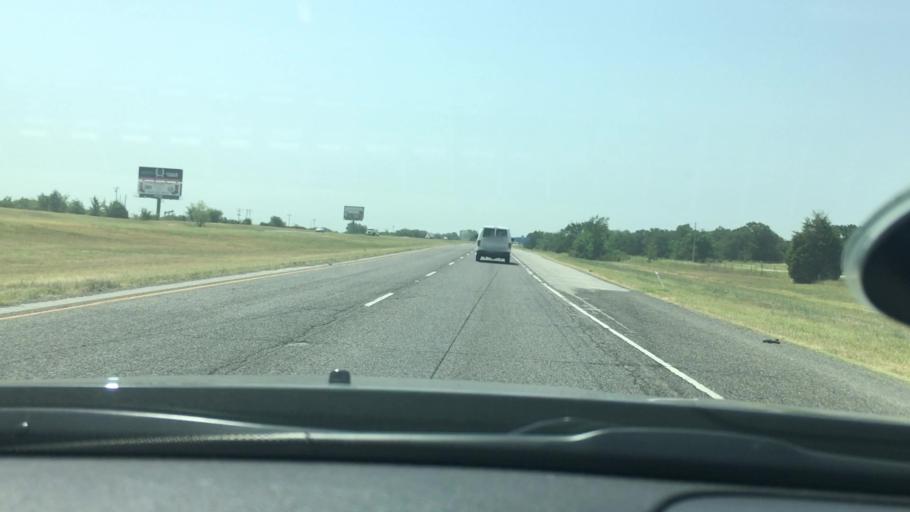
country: US
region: Oklahoma
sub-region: Garvin County
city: Wynnewood
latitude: 34.5662
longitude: -97.1968
